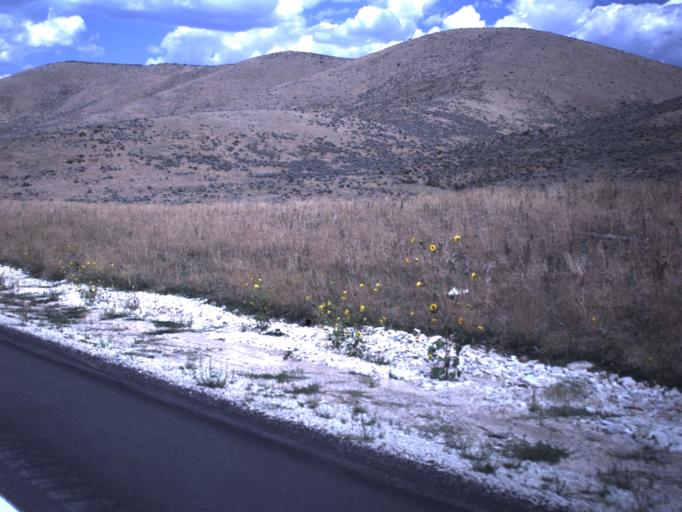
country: US
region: Utah
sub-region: Wasatch County
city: Midway
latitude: 40.4205
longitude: -111.4893
